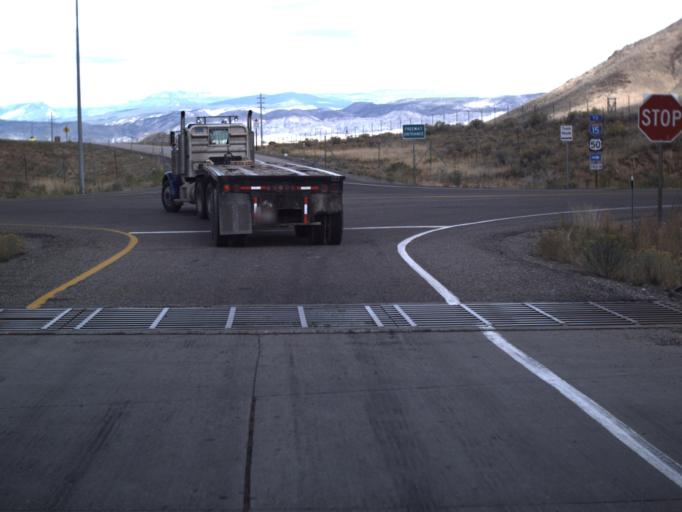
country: US
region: Utah
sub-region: Sevier County
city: Aurora
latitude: 38.8731
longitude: -111.9657
